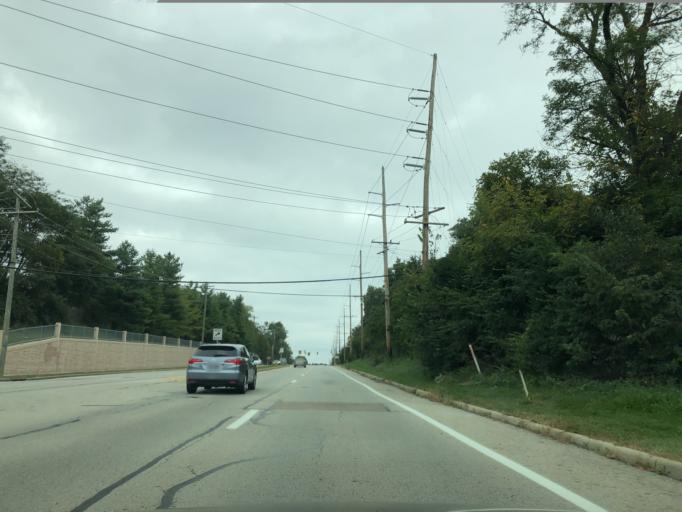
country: US
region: Ohio
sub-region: Hamilton County
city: Sixteen Mile Stand
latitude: 39.2760
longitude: -84.3239
